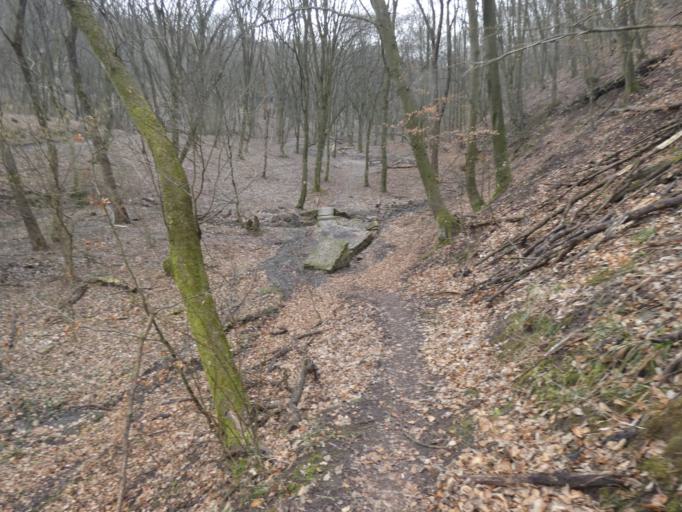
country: HU
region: Pest
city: Kismaros
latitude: 47.8428
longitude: 18.9976
